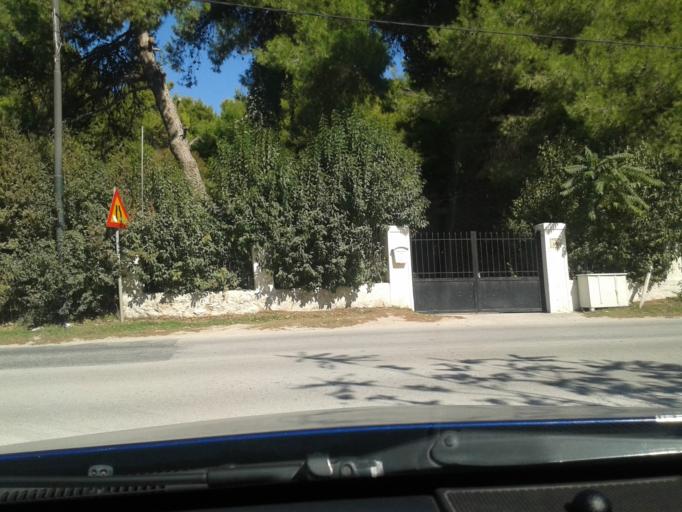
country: GR
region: Attica
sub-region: Nomarchia Anatolikis Attikis
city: Dionysos
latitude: 38.1008
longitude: 23.8850
